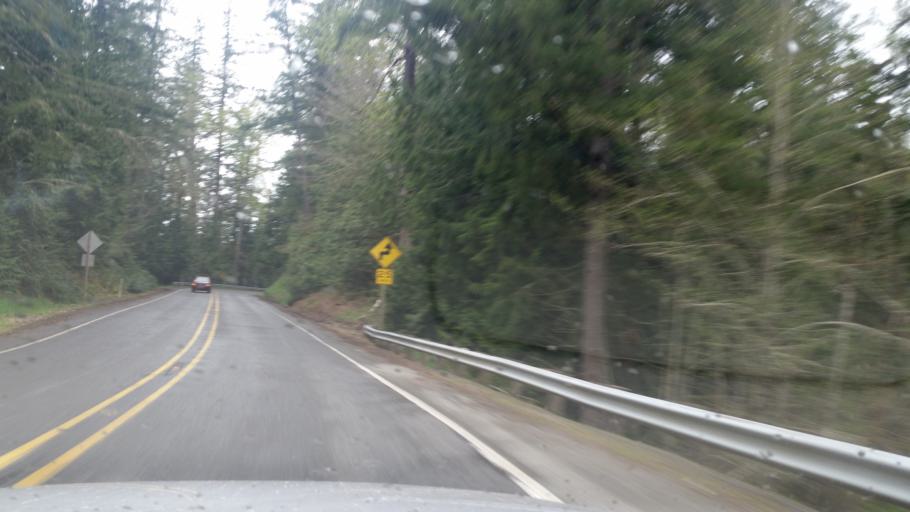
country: US
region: Washington
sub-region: Pierce County
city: Eatonville
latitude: 46.8570
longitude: -122.3032
